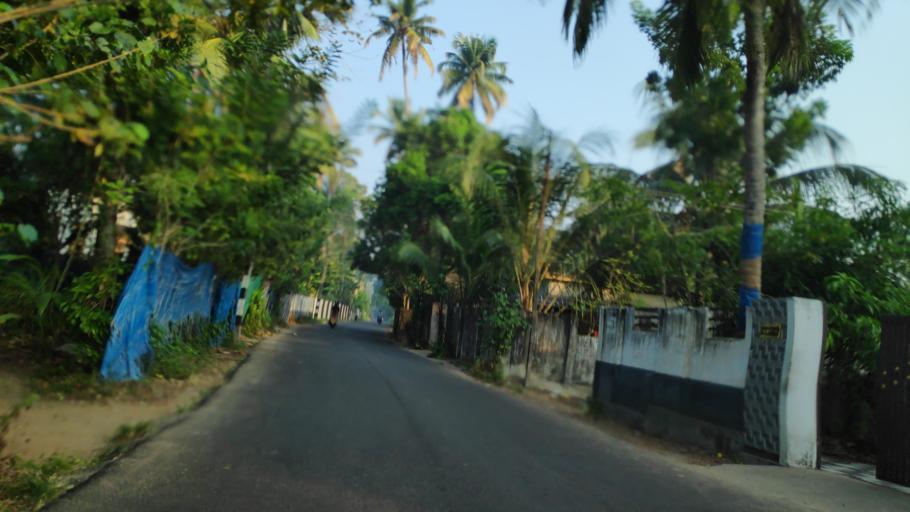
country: IN
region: Kerala
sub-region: Alappuzha
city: Vayalar
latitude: 9.6951
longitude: 76.2903
